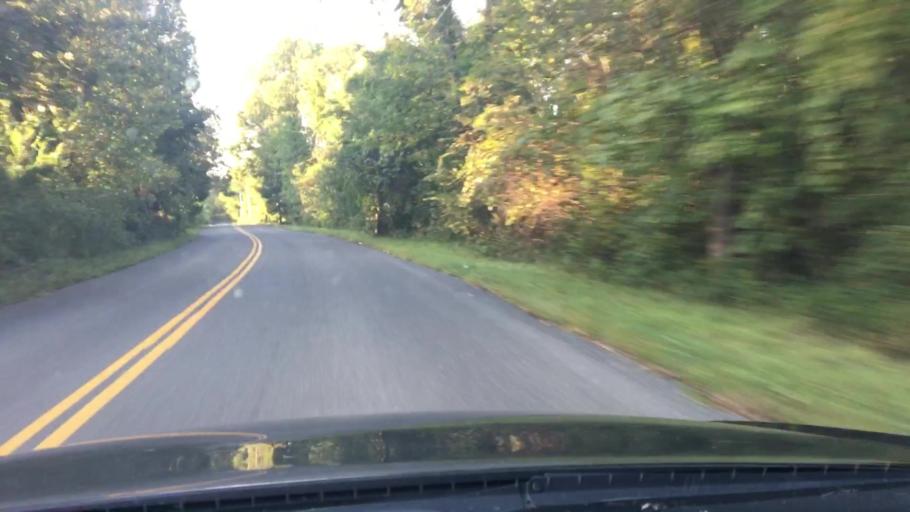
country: US
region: Connecticut
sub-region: Litchfield County
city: New Milford
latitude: 41.6034
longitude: -73.3708
